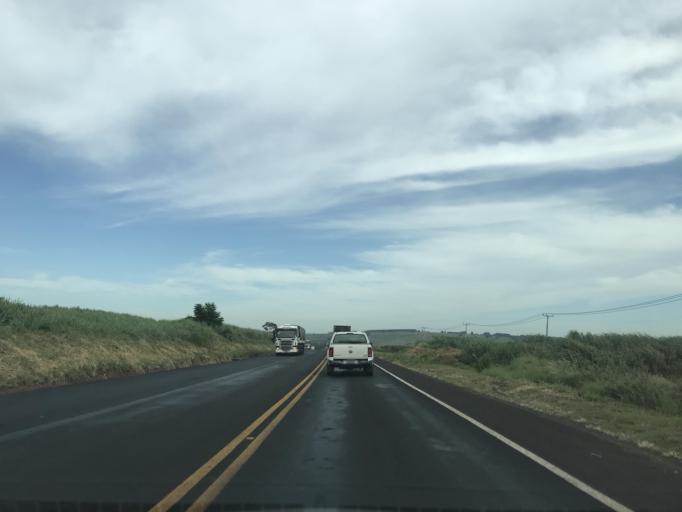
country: BR
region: Parana
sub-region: Paranavai
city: Paranavai
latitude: -23.0042
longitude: -52.5504
